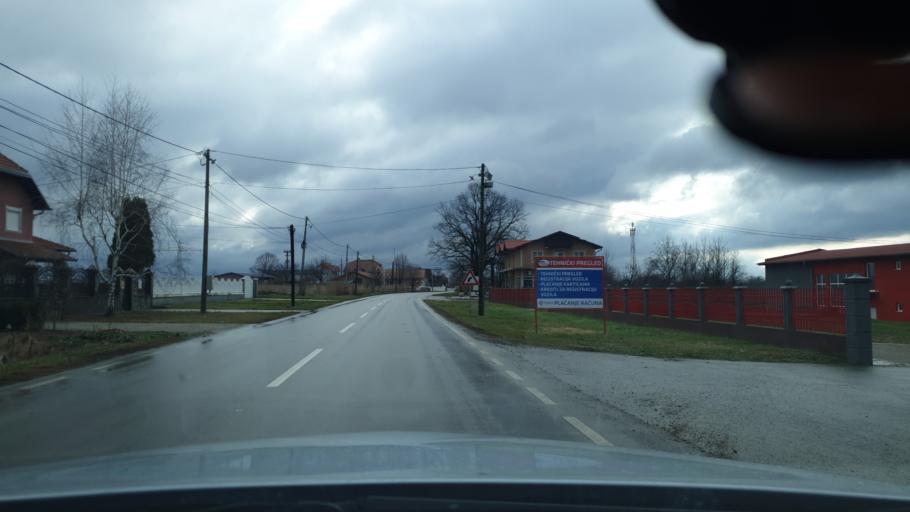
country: RS
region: Central Serbia
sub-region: Branicevski Okrug
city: Malo Crnice
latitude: 44.5648
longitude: 21.2957
